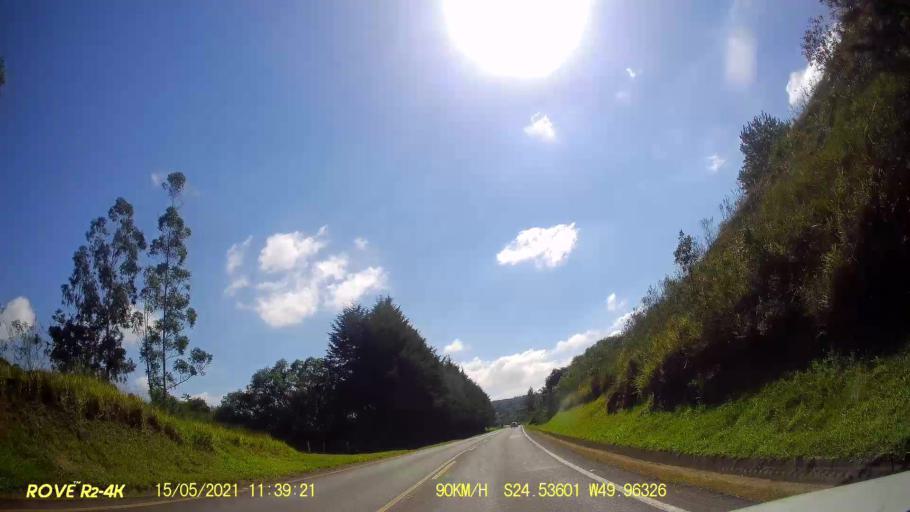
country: BR
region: Parana
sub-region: Pirai Do Sul
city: Pirai do Sul
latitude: -24.5364
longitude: -49.9629
